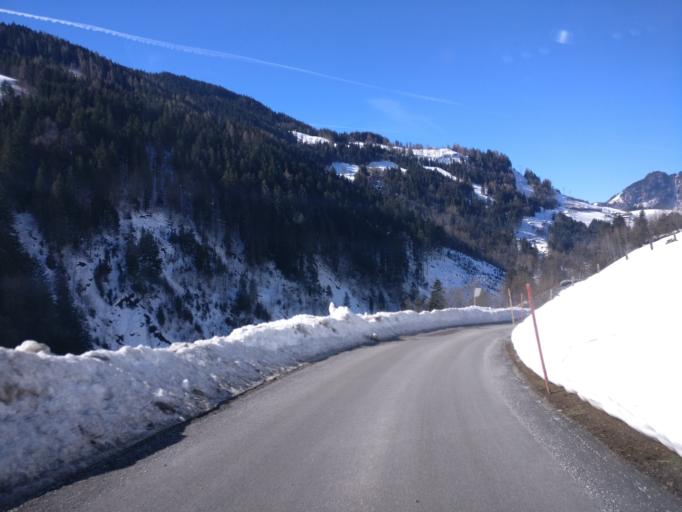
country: AT
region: Salzburg
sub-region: Politischer Bezirk Sankt Johann im Pongau
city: Sankt Johann im Pongau
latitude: 47.3312
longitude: 13.2333
